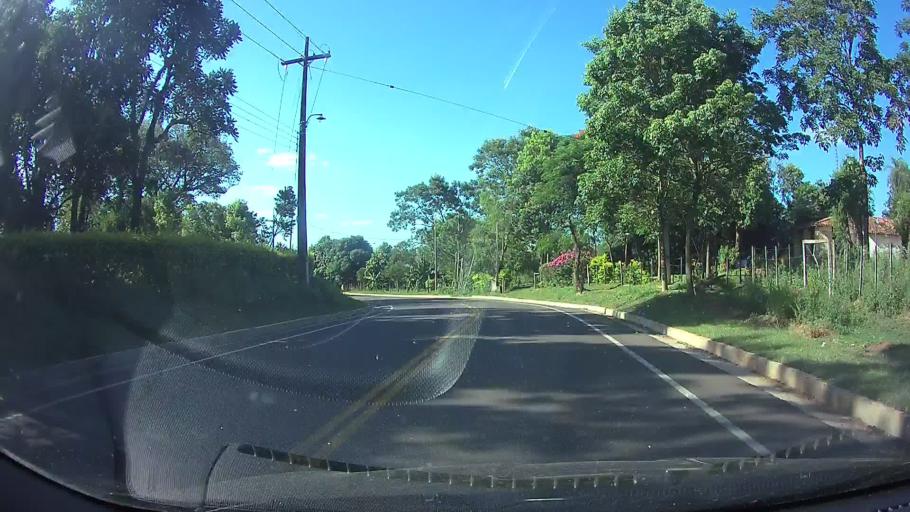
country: PY
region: Cordillera
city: Caacupe
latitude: -25.3455
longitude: -57.1527
